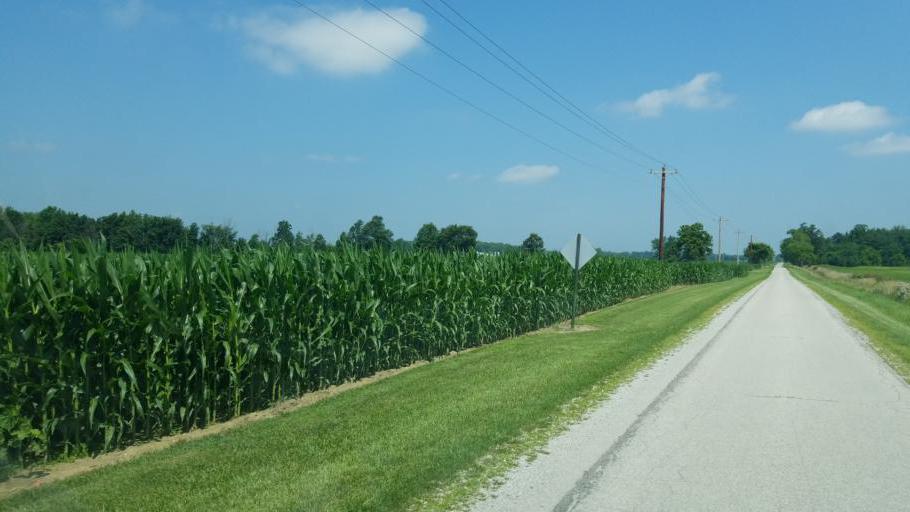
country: US
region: Ohio
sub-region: Crawford County
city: Bucyrus
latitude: 41.0246
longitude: -82.9775
